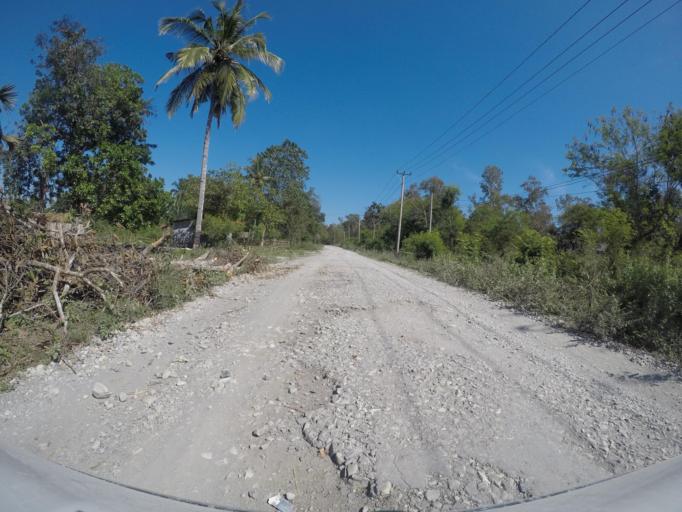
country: TL
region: Viqueque
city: Viqueque
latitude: -8.9728
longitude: 126.0608
